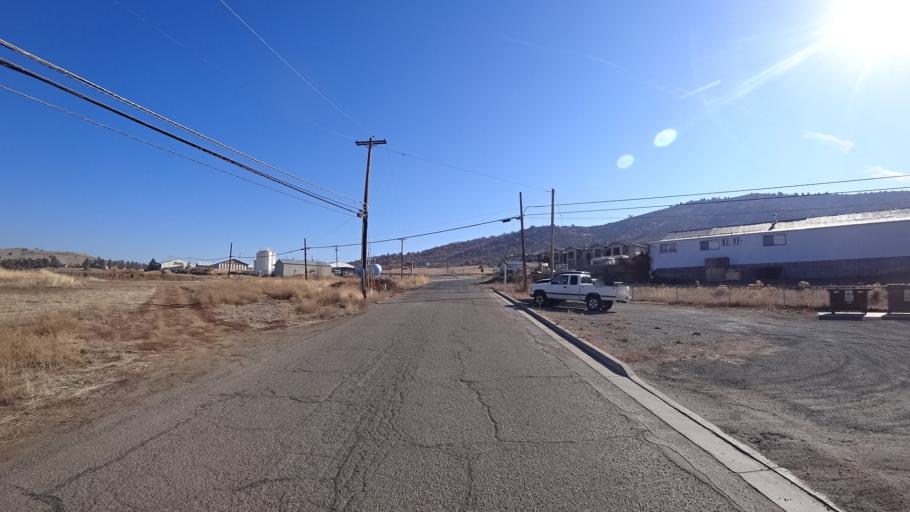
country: US
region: California
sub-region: Siskiyou County
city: Yreka
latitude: 41.7349
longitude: -122.6265
